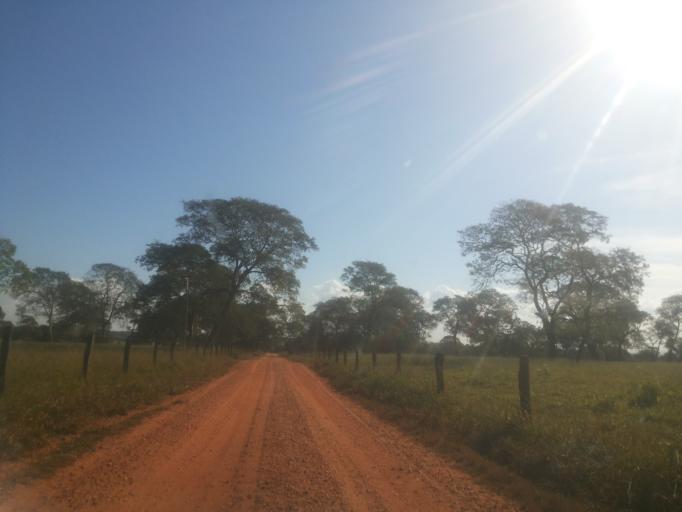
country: BR
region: Minas Gerais
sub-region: Santa Vitoria
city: Santa Vitoria
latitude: -19.0120
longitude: -50.4056
